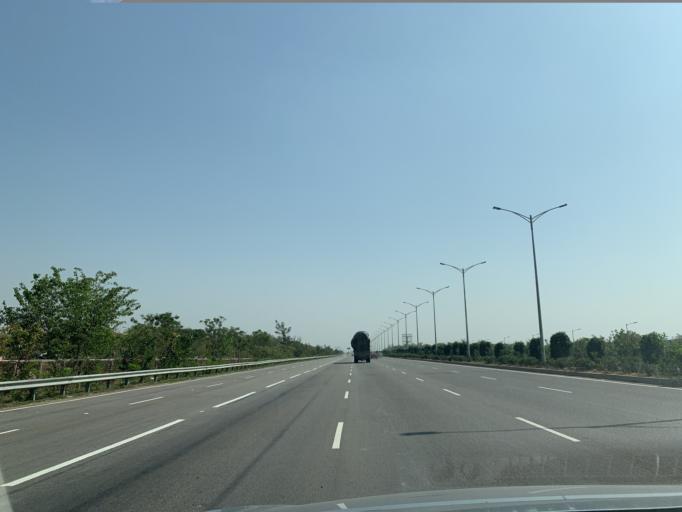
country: IN
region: Telangana
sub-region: Hyderabad
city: Hyderabad
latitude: 17.3593
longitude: 78.3549
